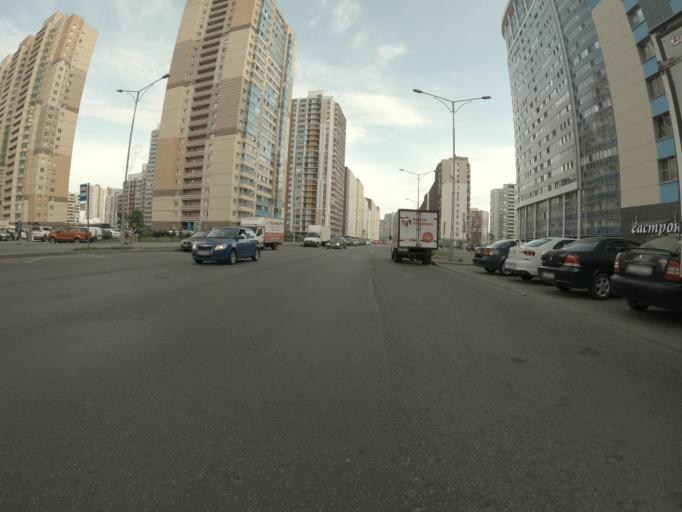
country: RU
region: Leningrad
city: Rybatskoye
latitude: 59.9038
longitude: 30.5127
